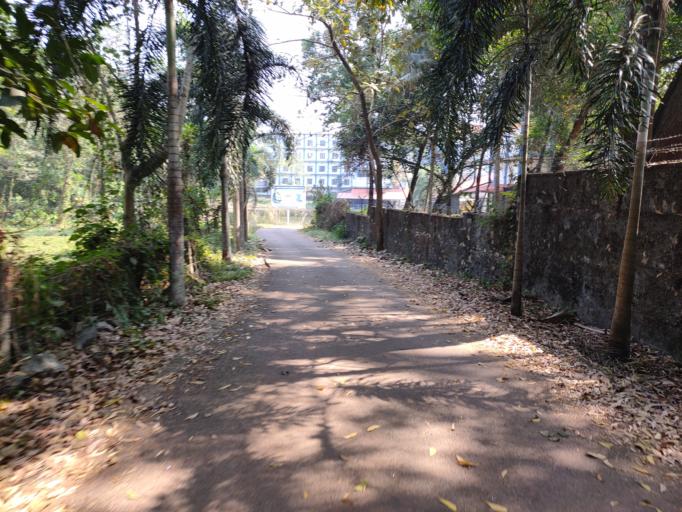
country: IN
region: Kerala
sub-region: Thrissur District
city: Kodungallur
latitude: 10.2338
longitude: 76.2776
